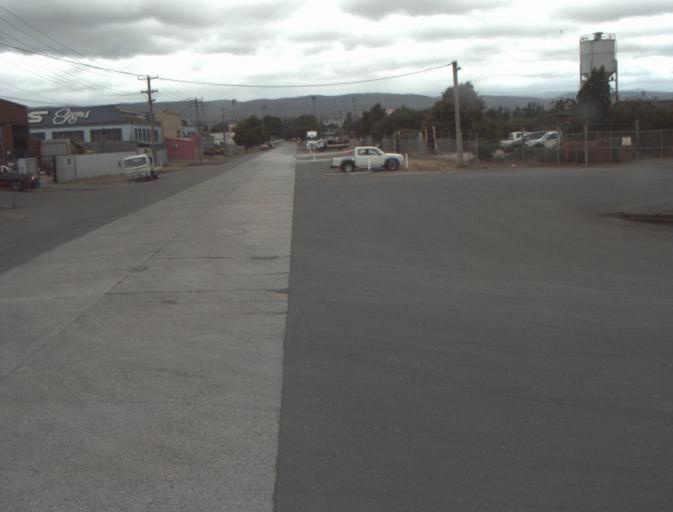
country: AU
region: Tasmania
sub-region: Launceston
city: Launceston
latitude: -41.4288
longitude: 147.1255
